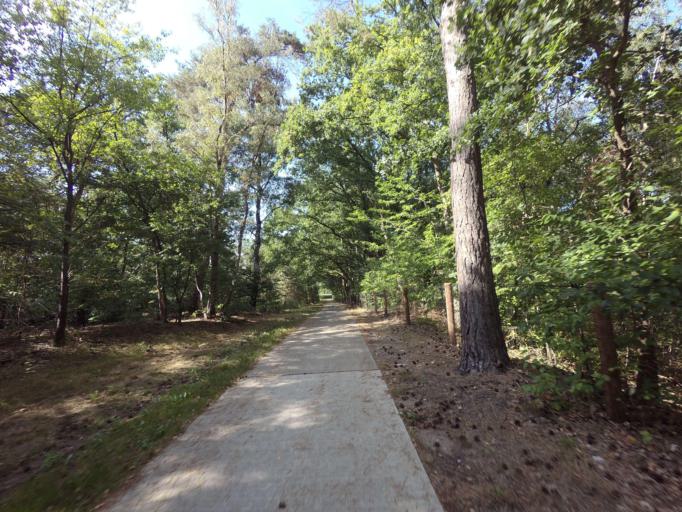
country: NL
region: Gelderland
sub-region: Gemeente Apeldoorn
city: Loenen
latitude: 52.1486
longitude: 6.0276
